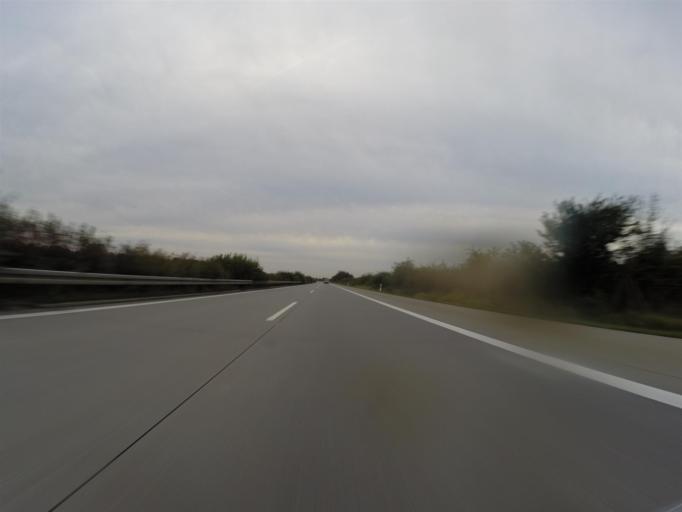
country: DE
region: Saxony-Anhalt
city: Lutzen
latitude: 51.2372
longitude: 12.1785
